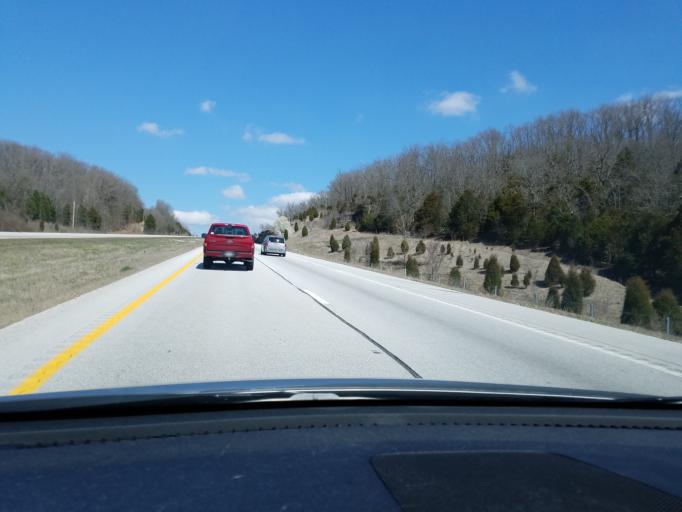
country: US
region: Missouri
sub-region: Christian County
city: Ozark
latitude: 36.8689
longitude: -93.2294
